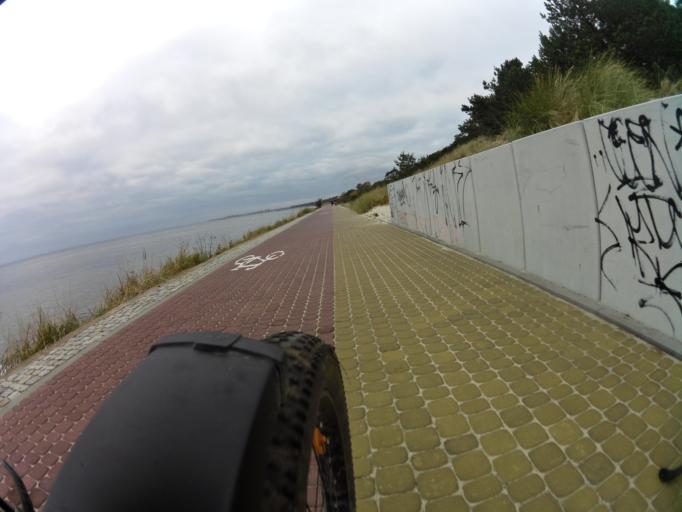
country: PL
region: Pomeranian Voivodeship
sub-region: Powiat pucki
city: Jastarnia
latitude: 54.6750
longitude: 18.7199
